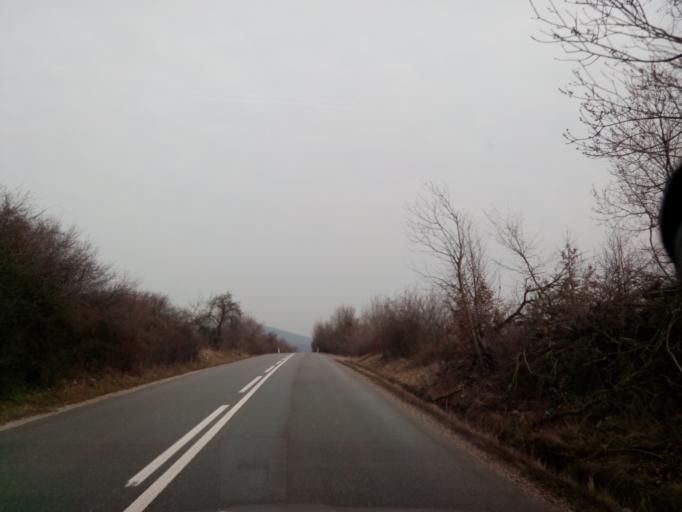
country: SK
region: Kosicky
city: Secovce
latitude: 48.6308
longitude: 21.5544
